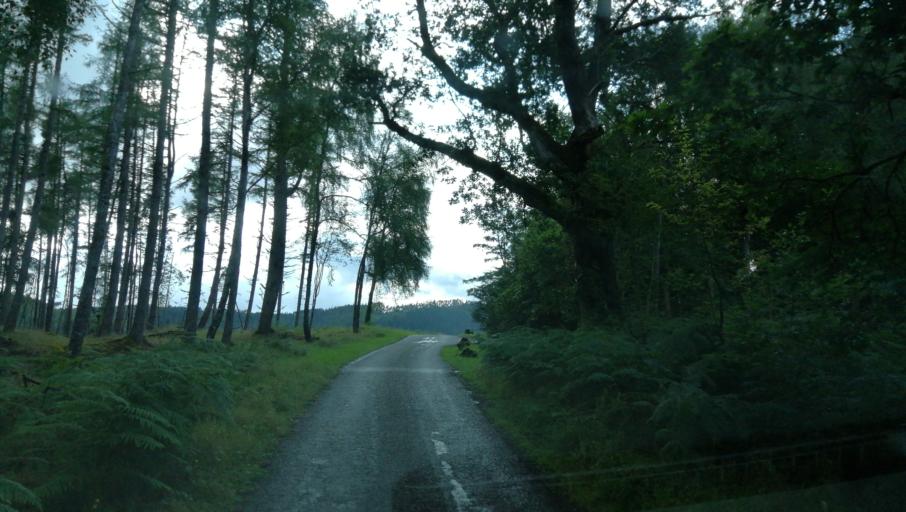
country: GB
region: Scotland
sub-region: Highland
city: Spean Bridge
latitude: 57.0700
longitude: -4.8274
